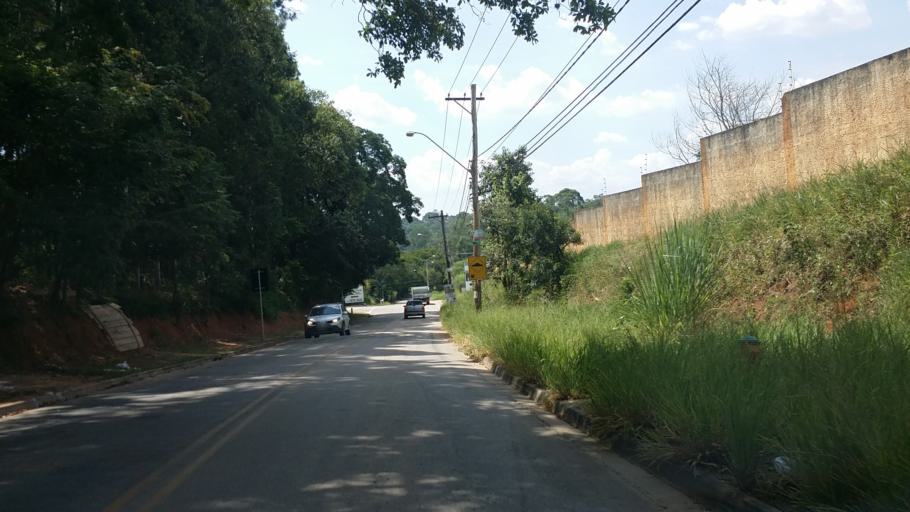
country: BR
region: Sao Paulo
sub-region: Itupeva
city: Itupeva
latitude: -23.2010
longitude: -47.0206
